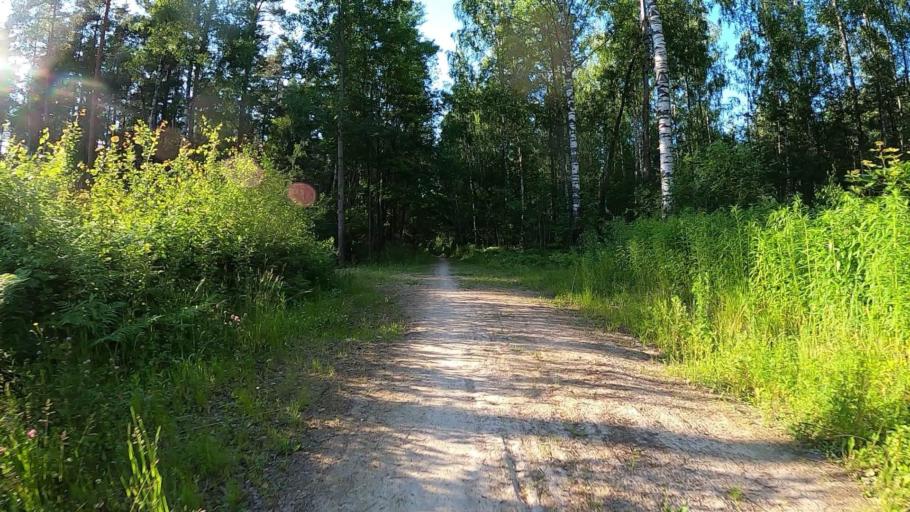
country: LV
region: Stopini
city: Ulbroka
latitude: 56.9271
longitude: 24.2344
